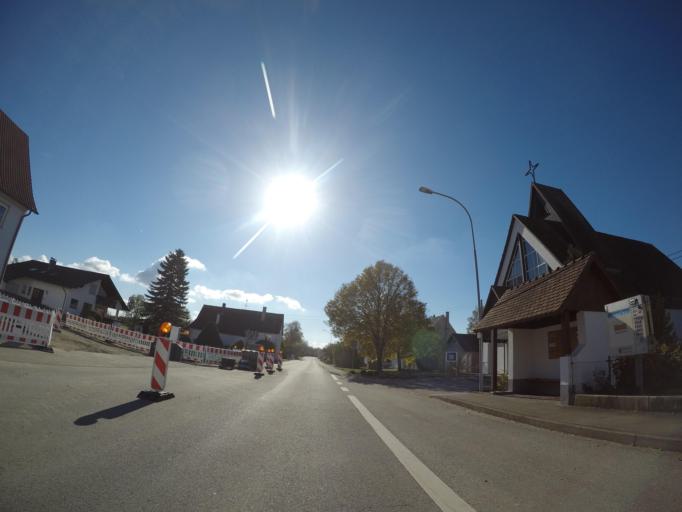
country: DE
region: Baden-Wuerttemberg
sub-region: Tuebingen Region
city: Bad Buchau
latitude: 48.0871
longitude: 9.5971
